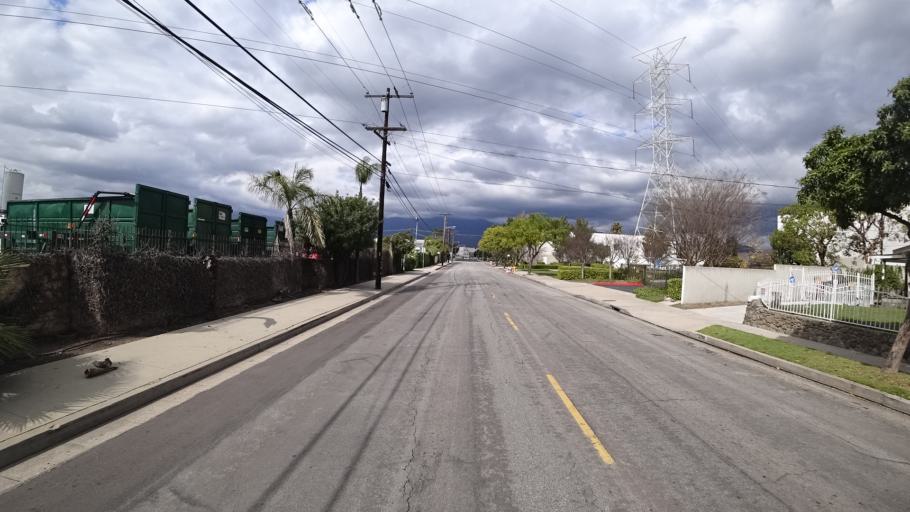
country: US
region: California
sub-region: Los Angeles County
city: Baldwin Park
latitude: 34.1053
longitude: -117.9694
